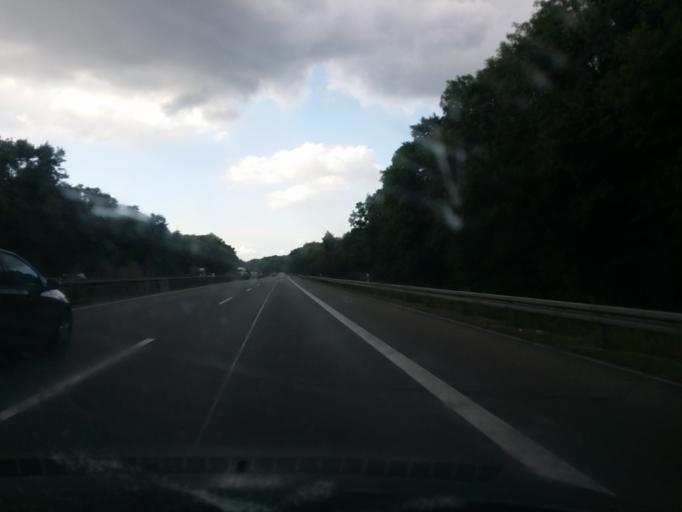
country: DE
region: Hesse
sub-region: Regierungsbezirk Darmstadt
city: Nauheim
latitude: 49.9456
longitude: 8.4779
